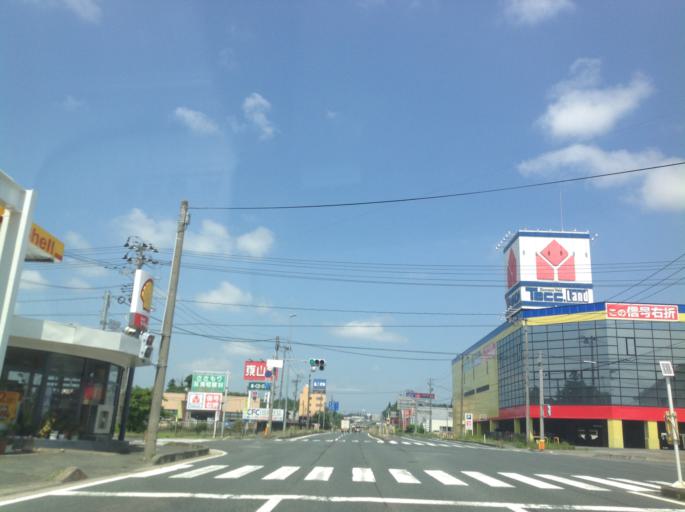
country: JP
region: Iwate
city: Kitakami
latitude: 39.2994
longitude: 141.1072
